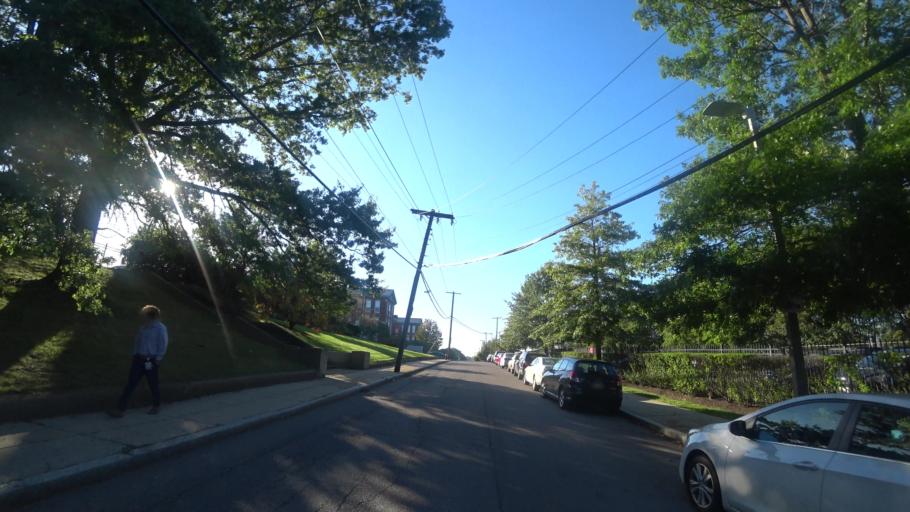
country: US
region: Massachusetts
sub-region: Norfolk County
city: Brookline
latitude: 42.3296
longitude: -71.1050
